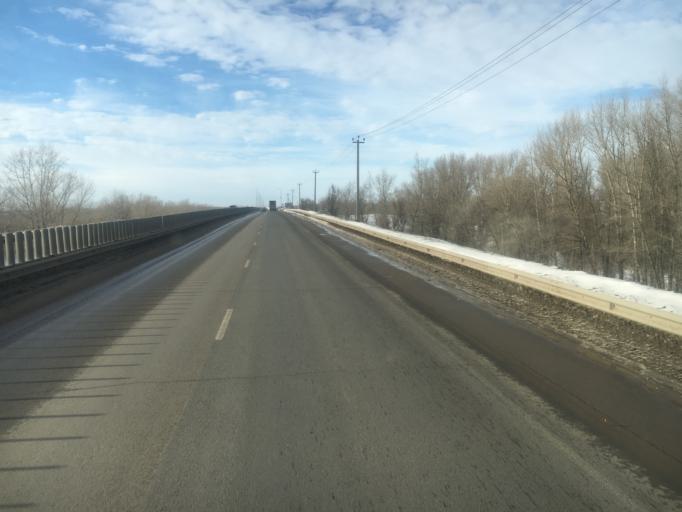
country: RU
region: Samara
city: Novosemeykino
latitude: 53.4294
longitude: 50.3052
